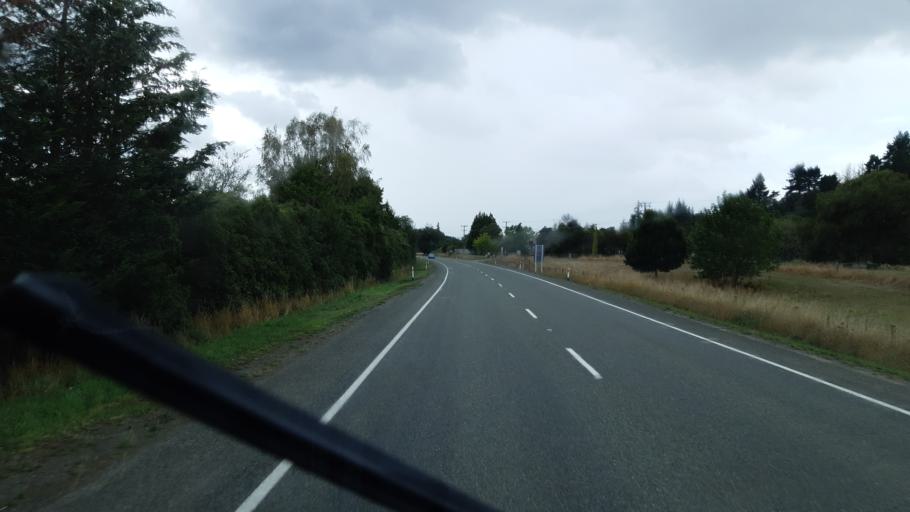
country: NZ
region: Tasman
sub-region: Tasman District
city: Wakefield
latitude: -41.4105
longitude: 173.0226
